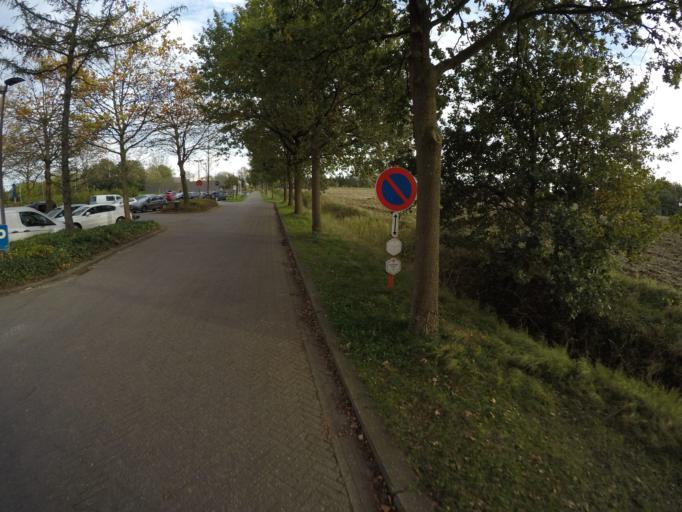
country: BE
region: Flanders
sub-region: Provincie Oost-Vlaanderen
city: Stekene
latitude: 51.1555
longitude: 4.0485
